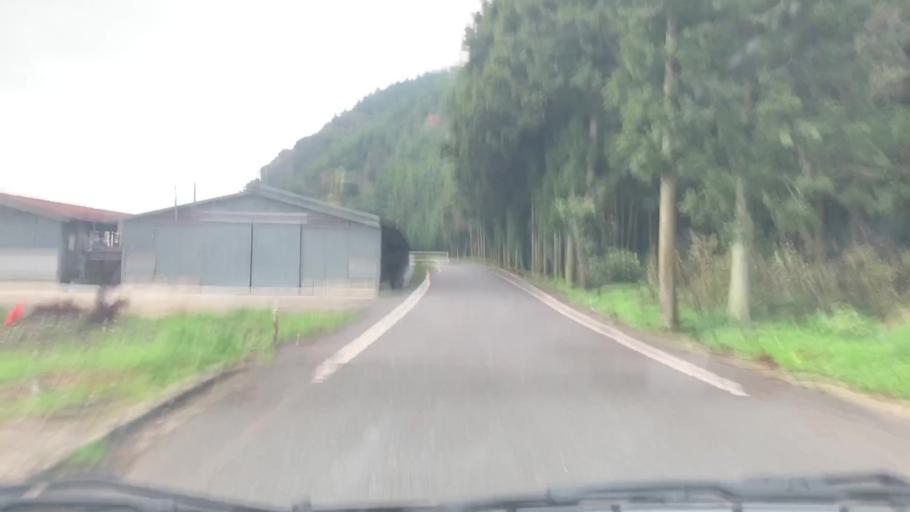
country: JP
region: Saga Prefecture
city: Ureshinomachi-shimojuku
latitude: 33.1238
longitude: 130.0459
